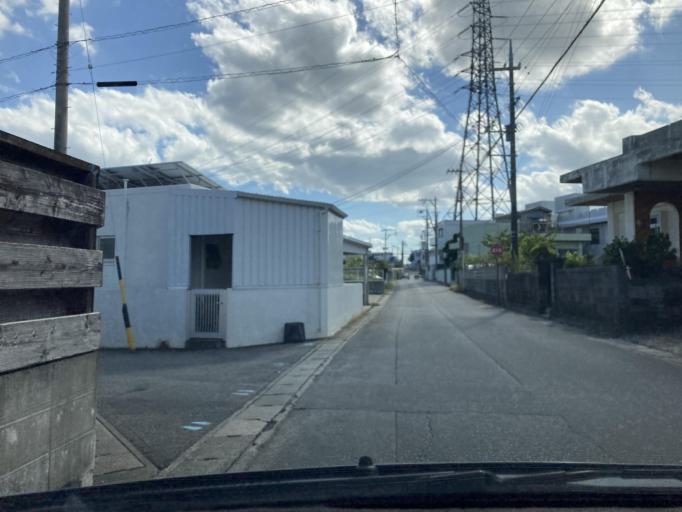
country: JP
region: Okinawa
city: Gushikawa
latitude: 26.3589
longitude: 127.8488
